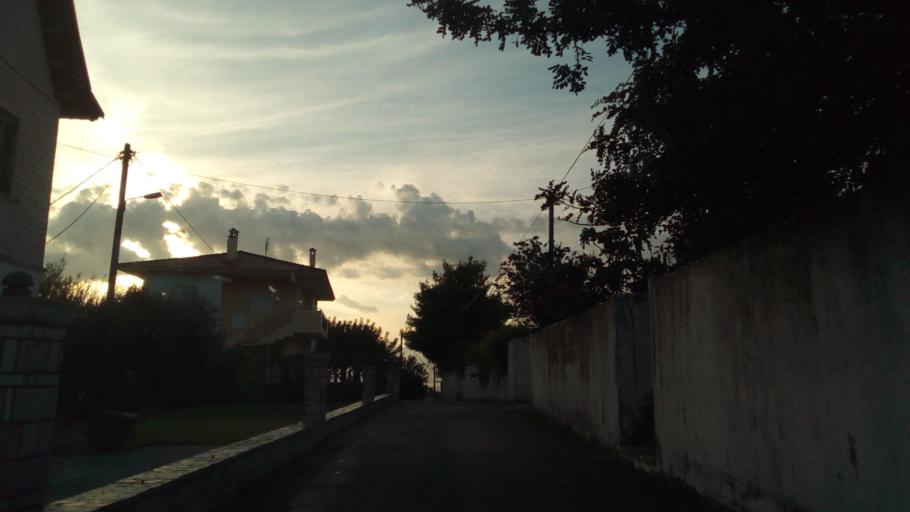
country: GR
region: West Greece
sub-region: Nomos Aitolias kai Akarnanias
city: Nafpaktos
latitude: 38.3896
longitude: 21.8063
